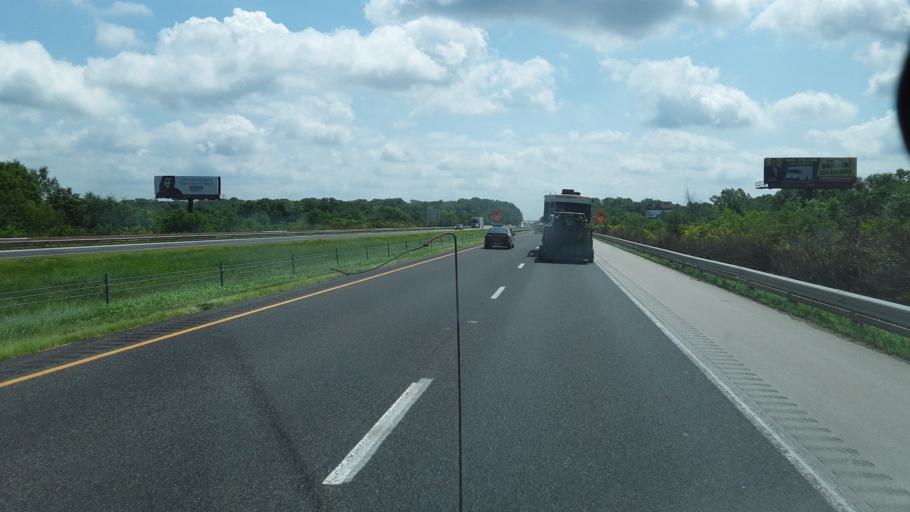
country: US
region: Indiana
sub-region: Vigo County
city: Terre Haute
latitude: 39.4308
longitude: -87.3819
